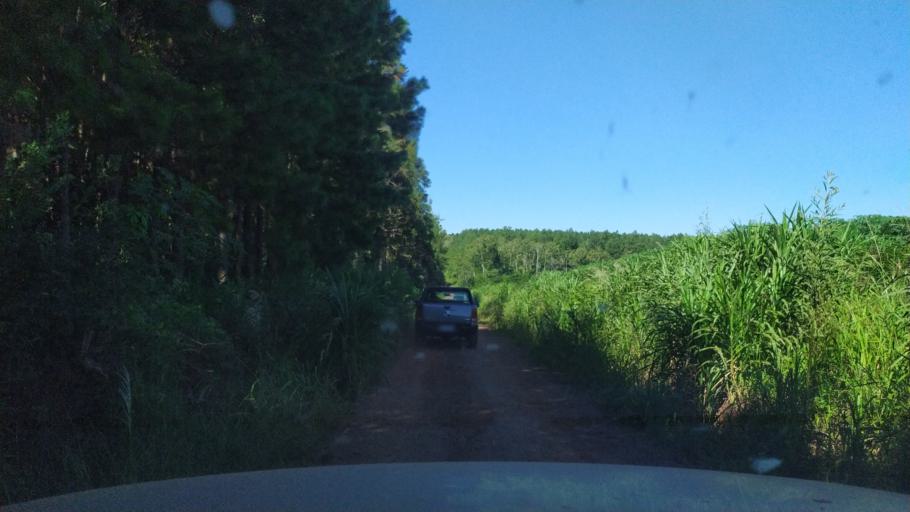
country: AR
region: Misiones
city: Caraguatay
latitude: -26.6733
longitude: -54.6980
